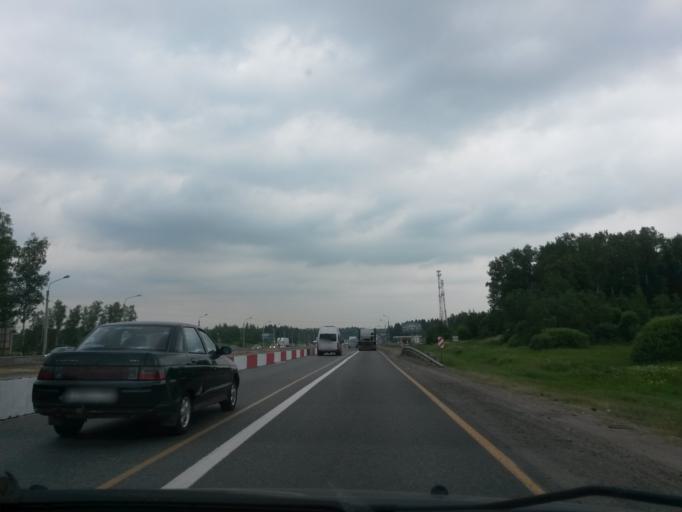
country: RU
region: Moskovskaya
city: Lyubuchany
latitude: 55.2252
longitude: 37.5315
